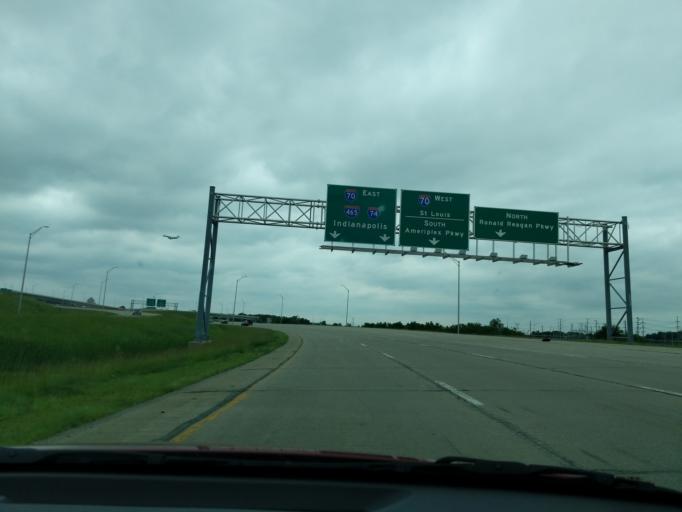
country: US
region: Indiana
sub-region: Hendricks County
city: Plainfield
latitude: 39.6966
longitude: -86.3200
